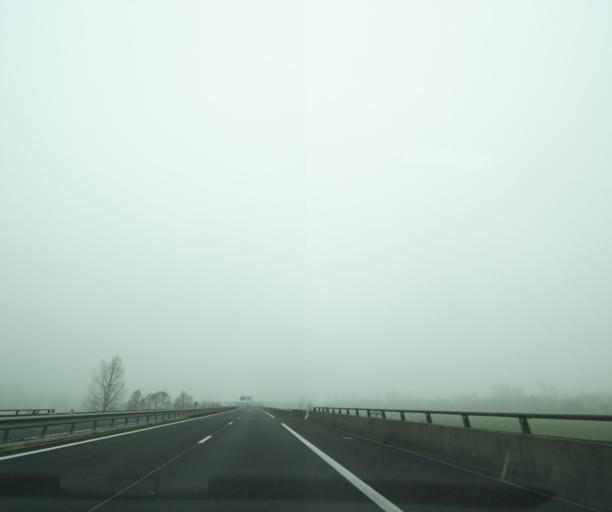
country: FR
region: Midi-Pyrenees
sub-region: Departement du Tarn-et-Garonne
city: Caussade
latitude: 44.1483
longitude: 1.5089
